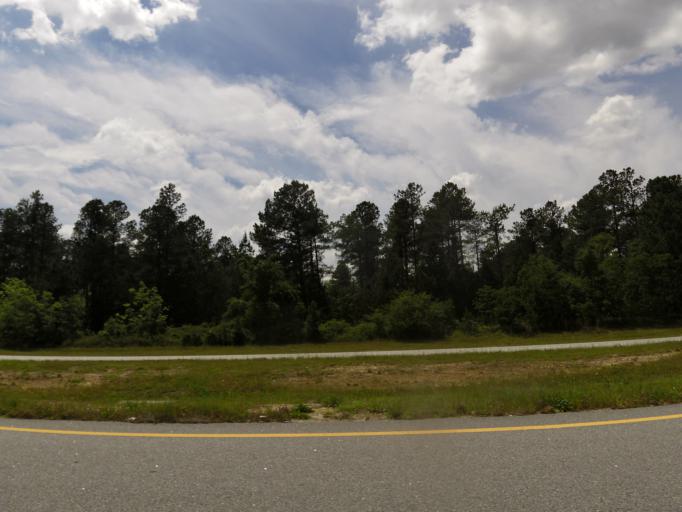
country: US
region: Georgia
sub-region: Emanuel County
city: Swainsboro
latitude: 32.6876
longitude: -82.3900
